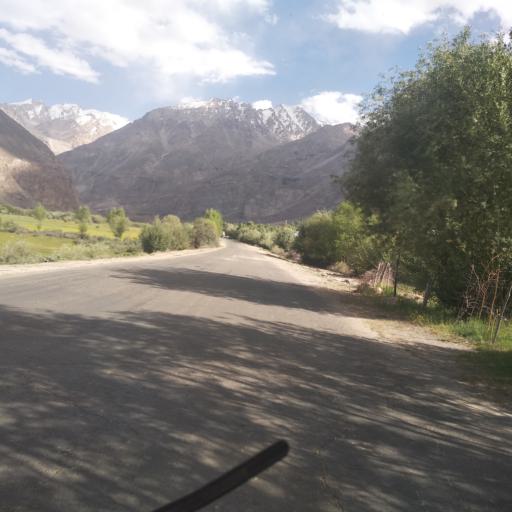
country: TJ
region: Gorno-Badakhshan
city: Roshtqal'a
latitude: 37.7279
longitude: 72.1597
